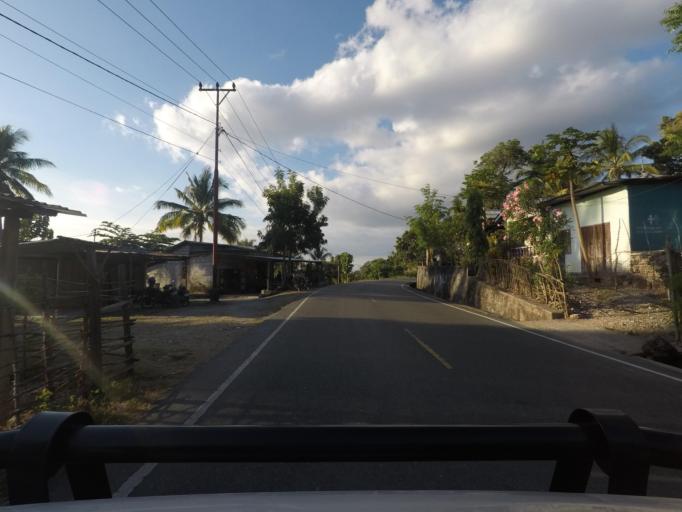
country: TL
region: Bobonaro
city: Maliana
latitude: -8.9641
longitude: 125.0532
